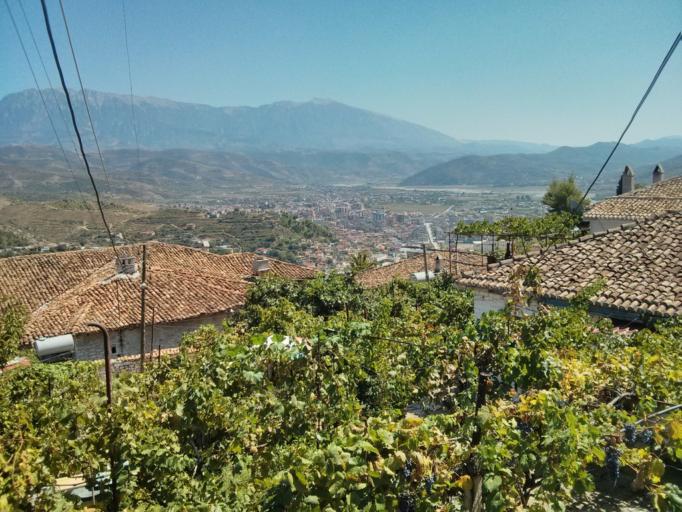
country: AL
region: Berat
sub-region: Rrethi i Beratit
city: Berat
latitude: 40.7078
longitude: 19.9461
